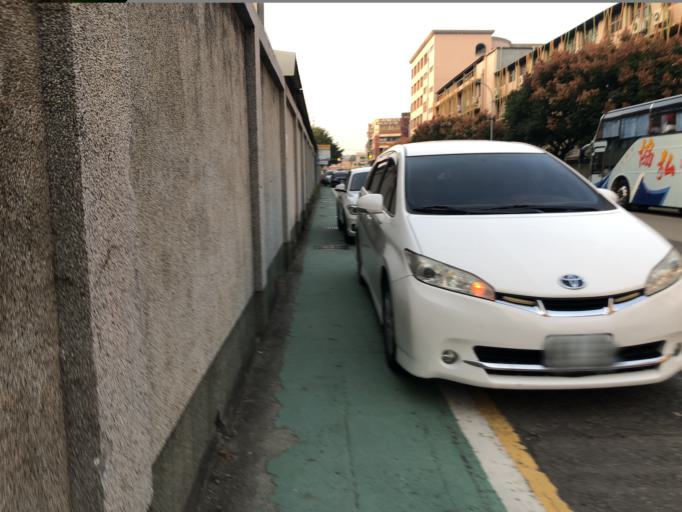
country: TW
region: Taiwan
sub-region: Taichung City
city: Taichung
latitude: 24.1368
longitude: 120.6102
